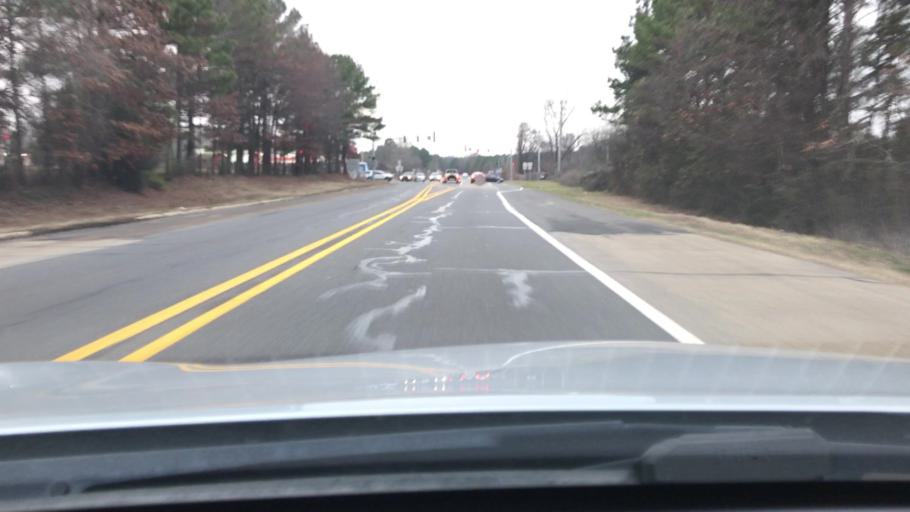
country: US
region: Arkansas
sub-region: Hempstead County
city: Hope
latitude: 33.6695
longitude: -93.5758
